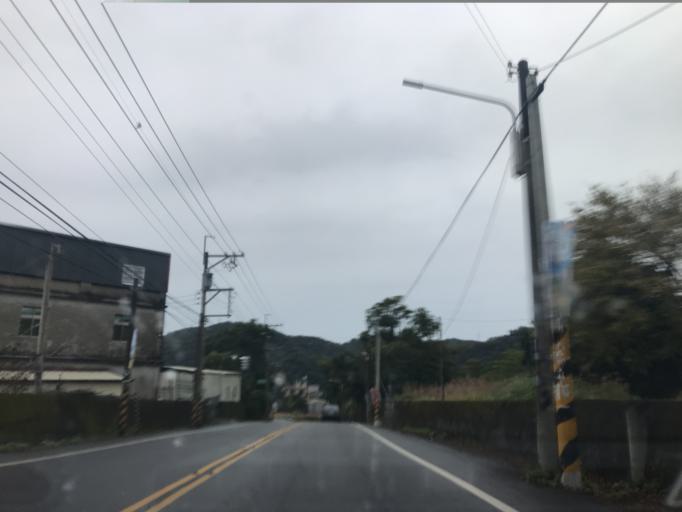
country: TW
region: Taiwan
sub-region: Hsinchu
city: Zhubei
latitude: 24.8386
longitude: 121.1069
